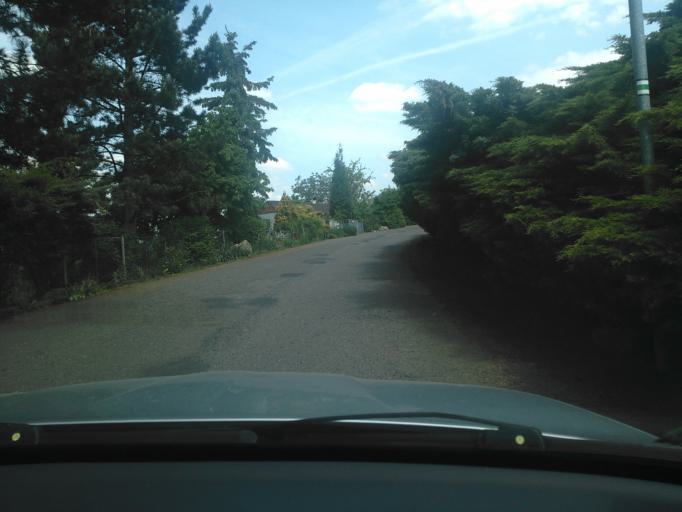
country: CZ
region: Ustecky
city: Becov
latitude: 50.4664
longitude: 13.7554
